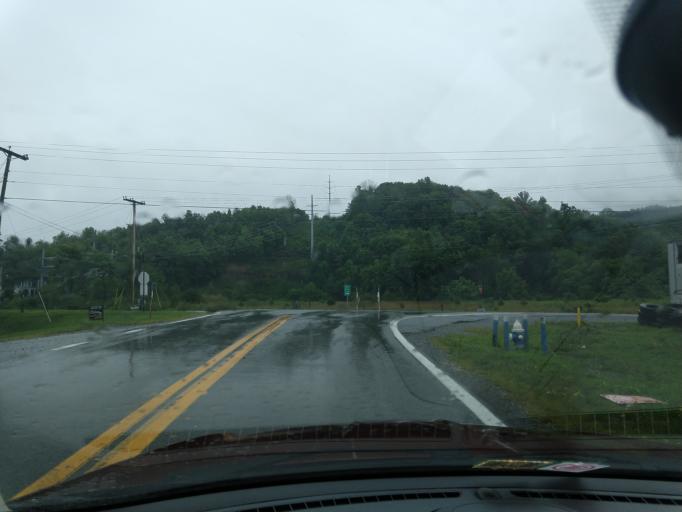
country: US
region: West Virginia
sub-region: Mercer County
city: Athens
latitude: 37.3629
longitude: -81.0372
